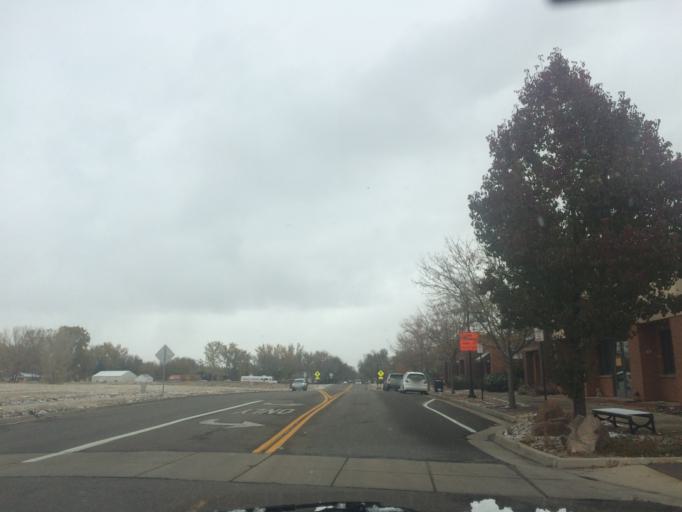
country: US
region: Colorado
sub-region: Boulder County
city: Erie
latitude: 40.0418
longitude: -105.0473
